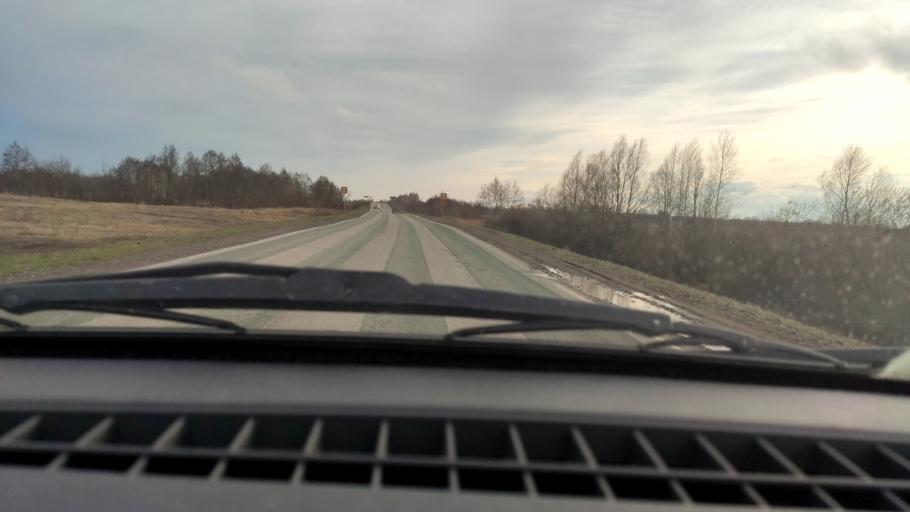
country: RU
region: Bashkortostan
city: Chishmy
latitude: 54.4441
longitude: 55.2422
